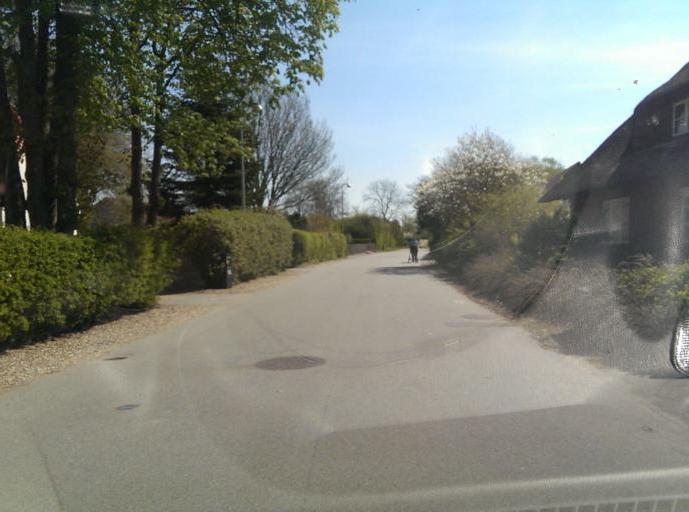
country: DK
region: South Denmark
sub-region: Esbjerg Kommune
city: Tjaereborg
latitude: 55.4607
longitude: 8.5873
